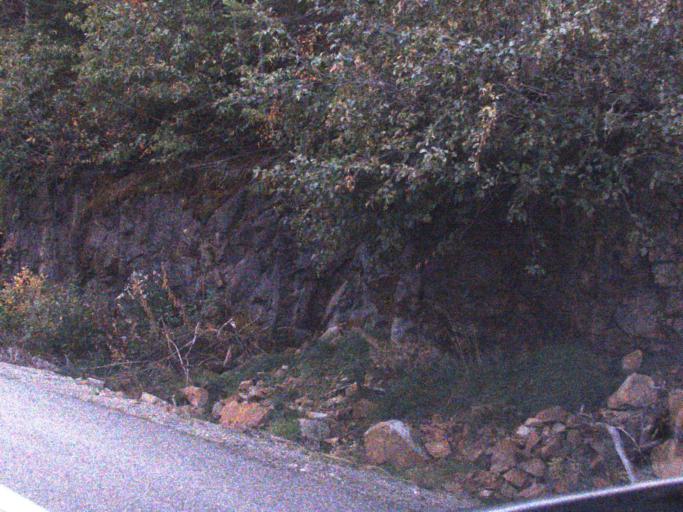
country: US
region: Washington
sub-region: Snohomish County
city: Darrington
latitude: 48.6370
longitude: -120.8504
